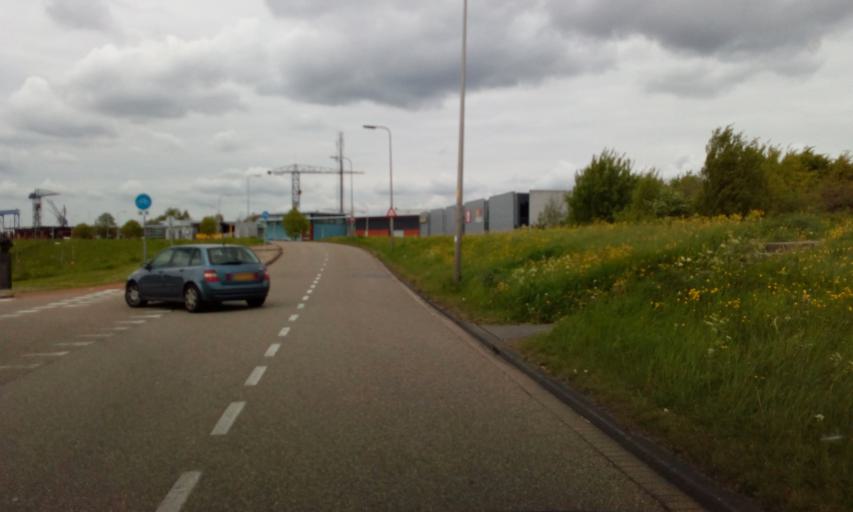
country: NL
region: South Holland
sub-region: Gemeente Capelle aan den IJssel
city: Capelle-West
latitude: 51.8990
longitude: 4.5815
